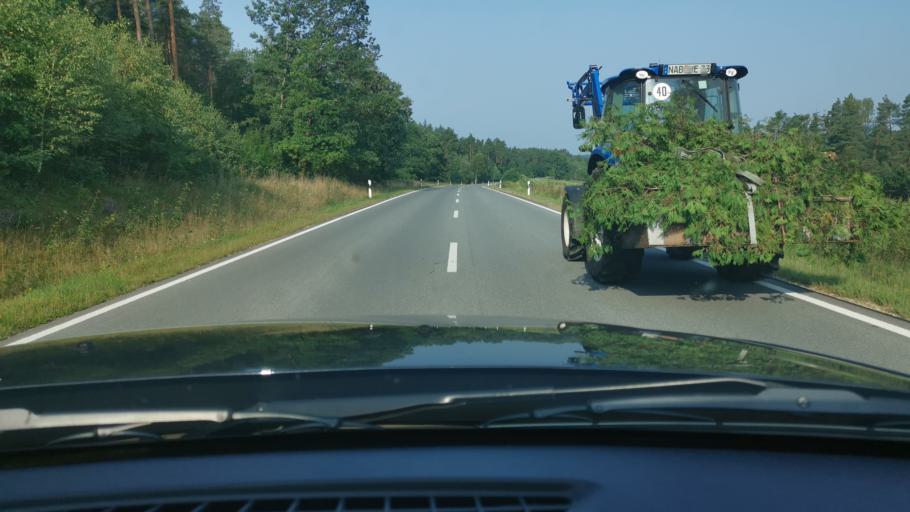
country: DE
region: Bavaria
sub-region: Upper Palatinate
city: Schnaittenbach
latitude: 49.5478
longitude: 12.0459
